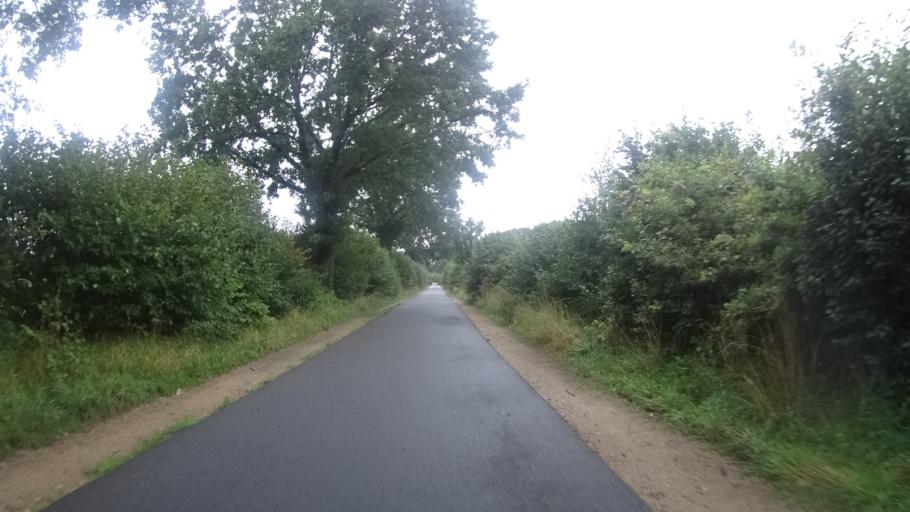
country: DE
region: Schleswig-Holstein
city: Siebeneichen
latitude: 53.5208
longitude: 10.6260
